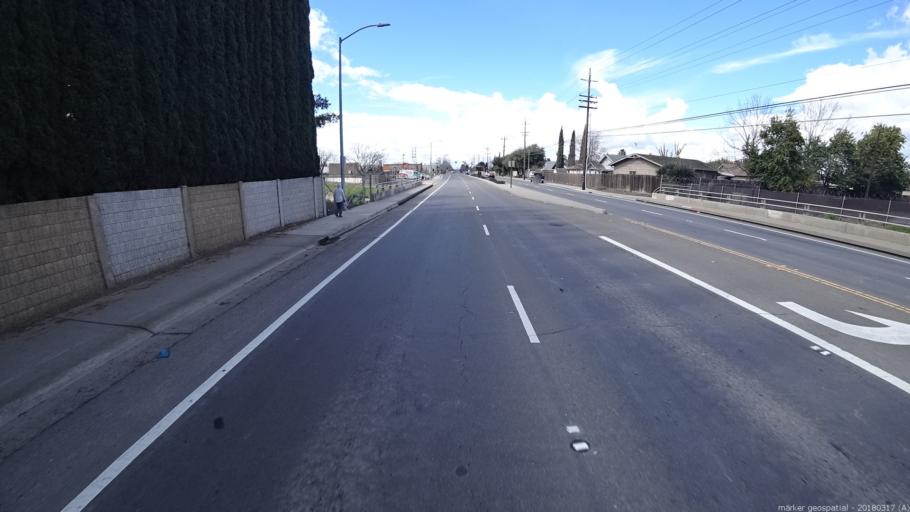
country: US
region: California
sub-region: Sacramento County
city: Florin
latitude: 38.4816
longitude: -121.4029
